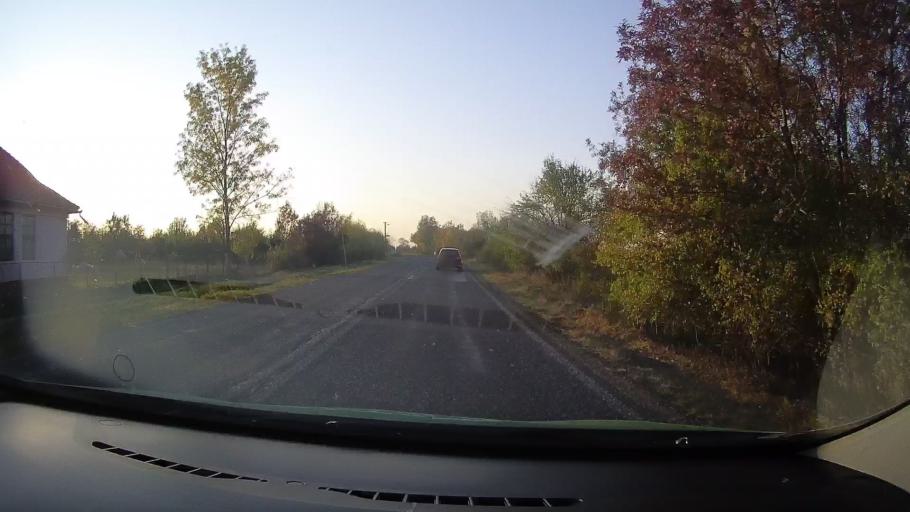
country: RO
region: Arad
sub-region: Comuna Bocsig
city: Bocsig
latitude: 46.4167
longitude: 21.9837
